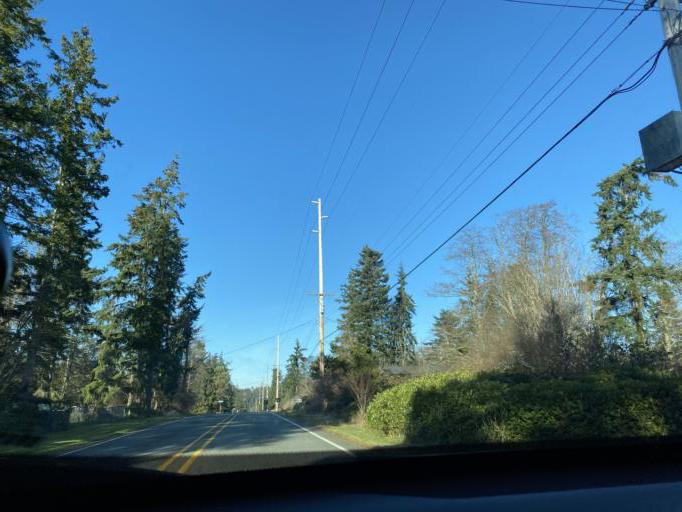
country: US
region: Washington
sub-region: Island County
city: Camano
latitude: 48.1245
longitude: -122.5643
